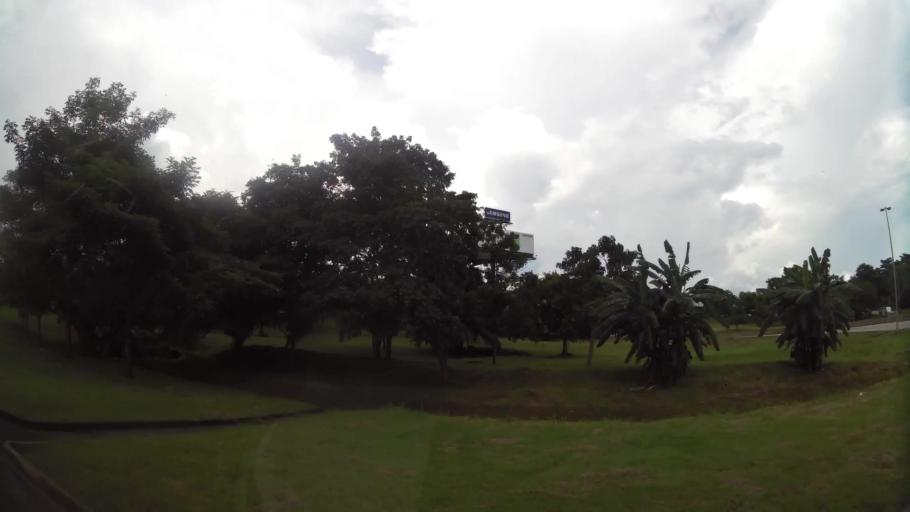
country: PA
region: Panama
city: Tocumen
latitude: 9.0684
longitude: -79.4047
